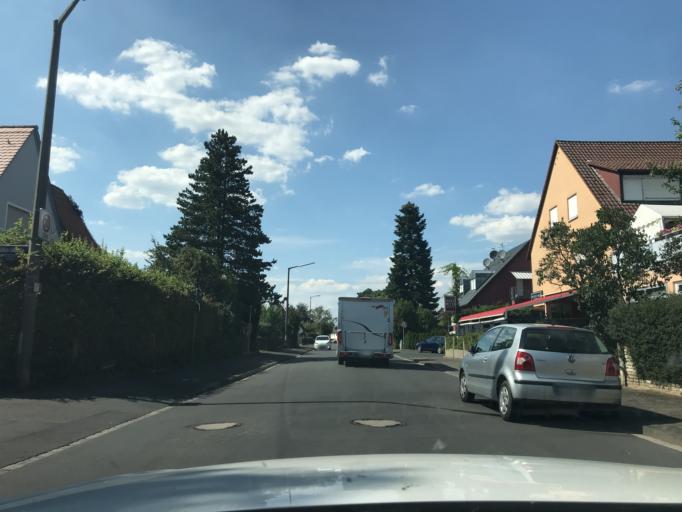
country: DE
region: Bavaria
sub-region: Regierungsbezirk Mittelfranken
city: Erlangen
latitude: 49.5648
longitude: 11.0047
